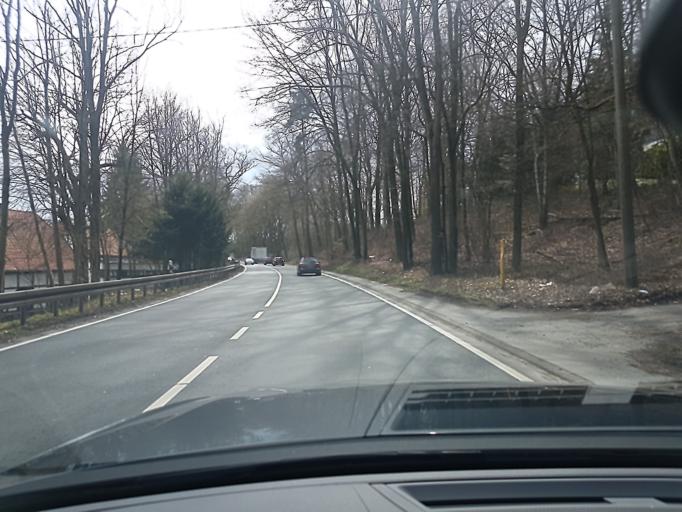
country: DE
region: North Rhine-Westphalia
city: Iserlohn
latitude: 51.4090
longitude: 7.6923
